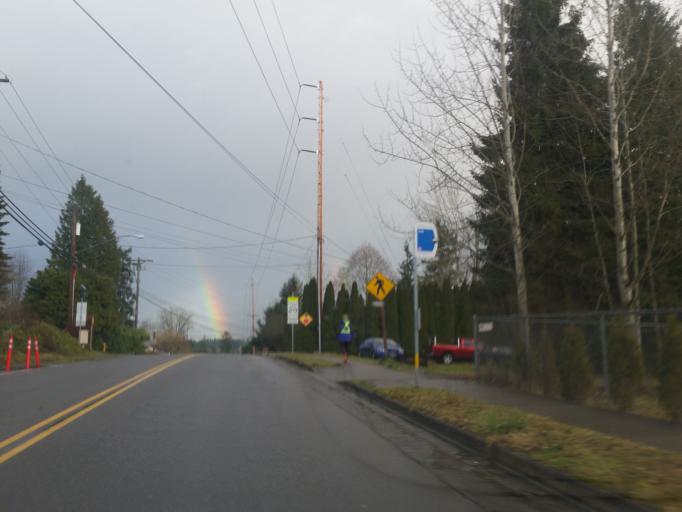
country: US
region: Washington
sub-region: Snohomish County
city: Brier
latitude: 47.7919
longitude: -122.2761
